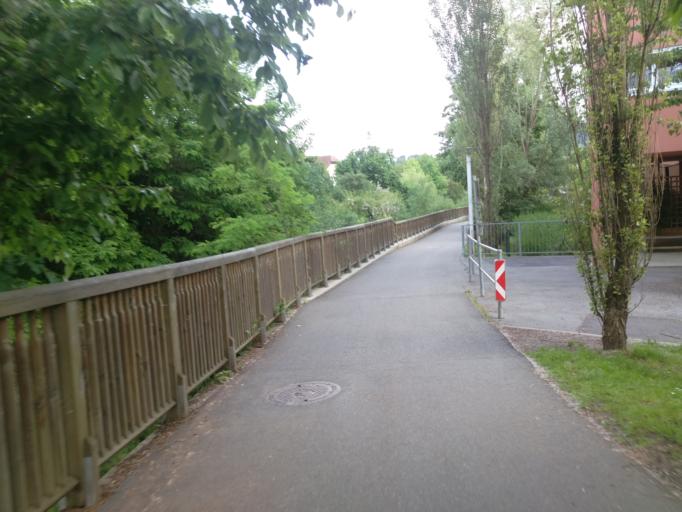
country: AT
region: Styria
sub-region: Politischer Bezirk Graz-Umgebung
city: Stattegg
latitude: 47.1075
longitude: 15.4251
